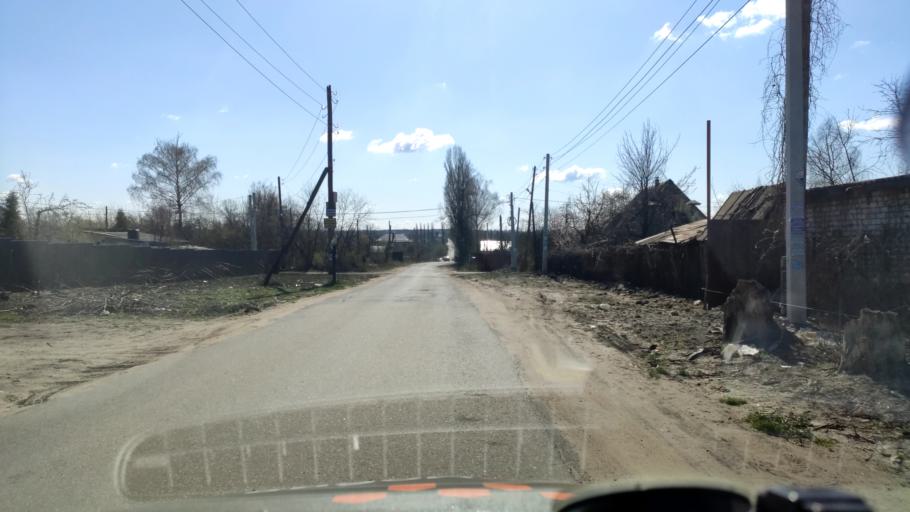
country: RU
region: Voronezj
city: Shilovo
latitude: 51.5982
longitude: 39.1471
